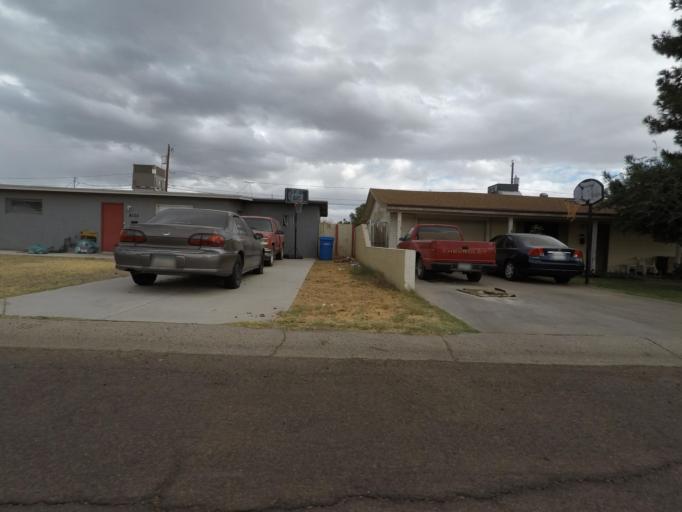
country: US
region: Arizona
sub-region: Maricopa County
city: Phoenix
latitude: 33.4964
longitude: -112.1222
